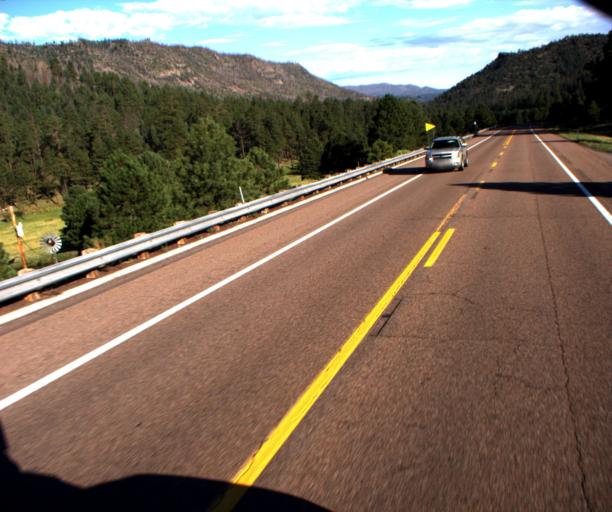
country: US
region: Arizona
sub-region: Apache County
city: Eagar
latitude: 33.9077
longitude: -109.1666
